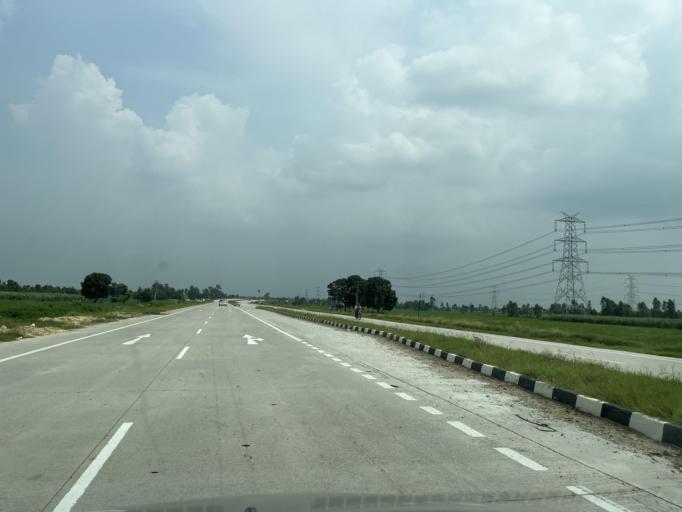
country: IN
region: Uttarakhand
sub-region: Udham Singh Nagar
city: Jaspur
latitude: 29.2921
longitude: 78.8479
